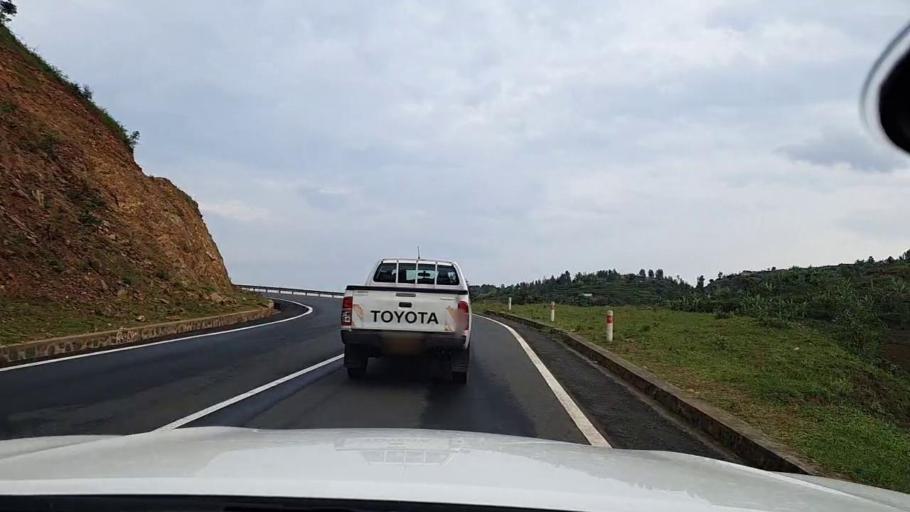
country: RW
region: Western Province
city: Kibuye
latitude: -2.1658
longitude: 29.2947
